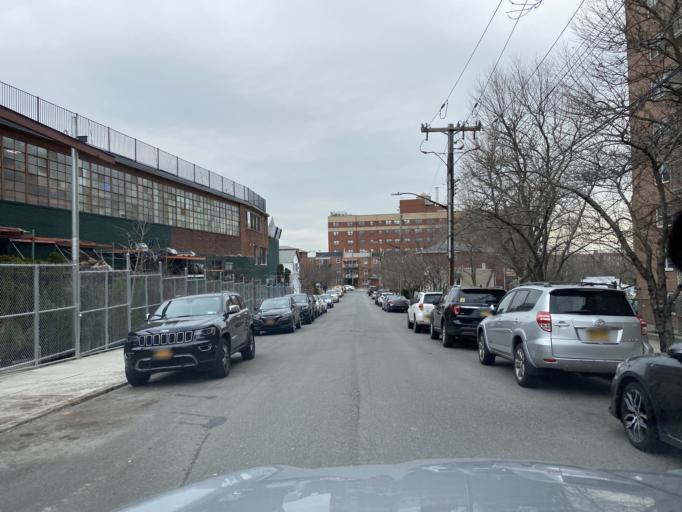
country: US
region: New York
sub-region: Queens County
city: Long Island City
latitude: 40.7394
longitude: -73.9074
